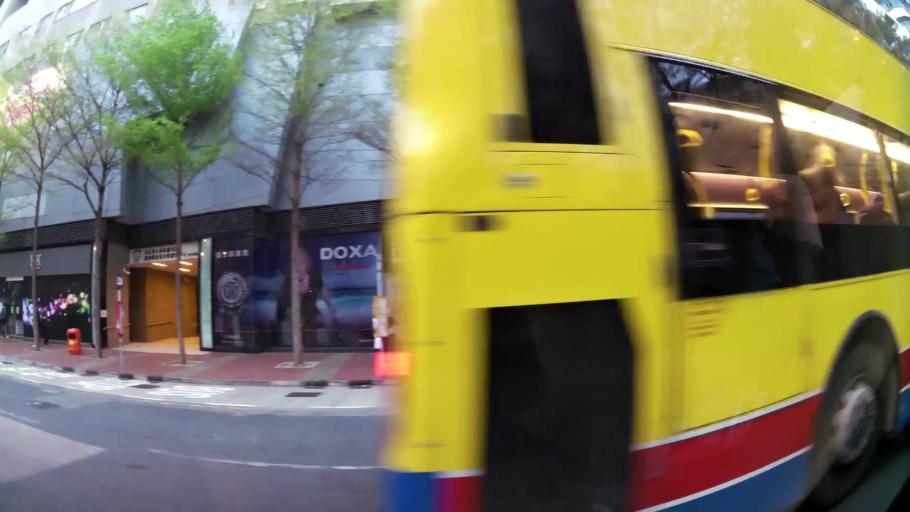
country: HK
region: Sham Shui Po
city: Sham Shui Po
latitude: 22.3188
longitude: 114.1620
